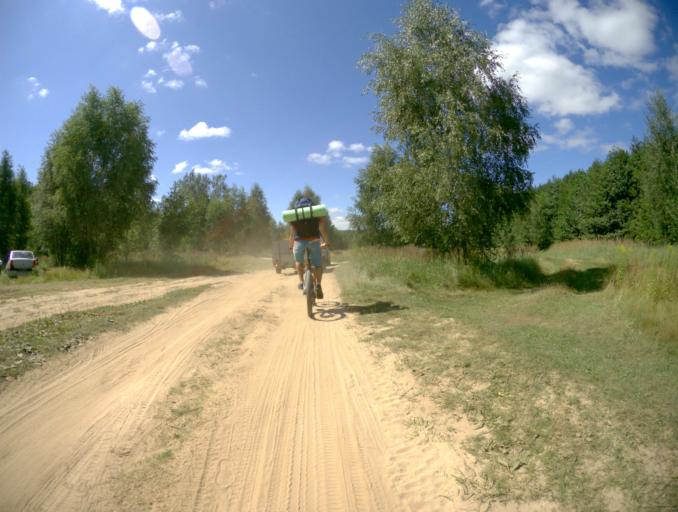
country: RU
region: Nizjnij Novgorod
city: Sitniki
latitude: 56.4575
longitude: 44.0114
